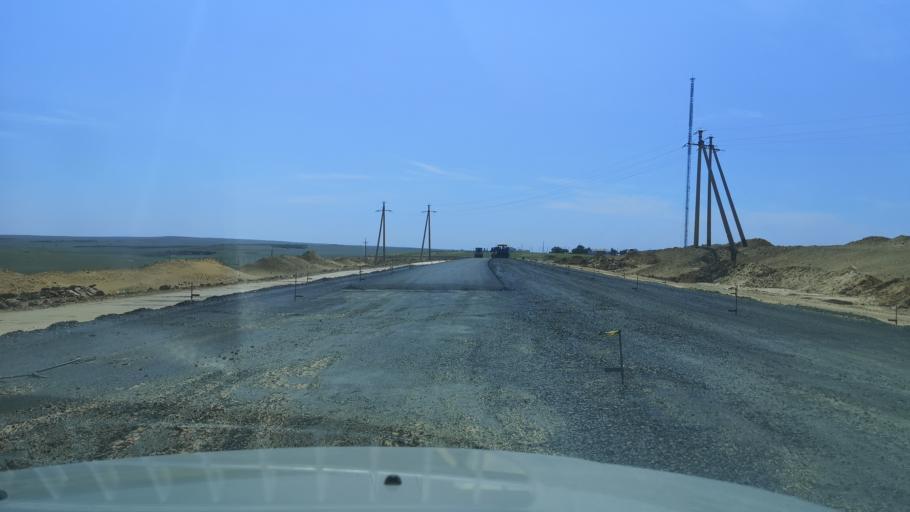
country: KZ
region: Aqtoebe
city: Bayganin
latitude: 48.6864
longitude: 55.8967
